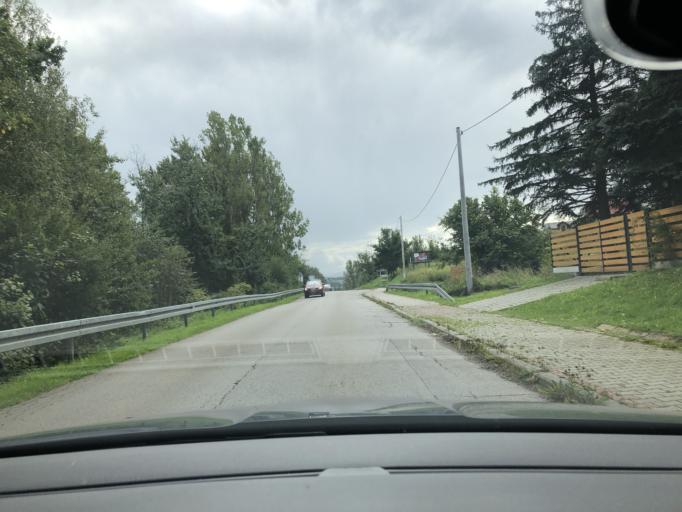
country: PL
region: Silesian Voivodeship
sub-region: Powiat zywiecki
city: Zarzecze
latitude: 49.7292
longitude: 19.1856
